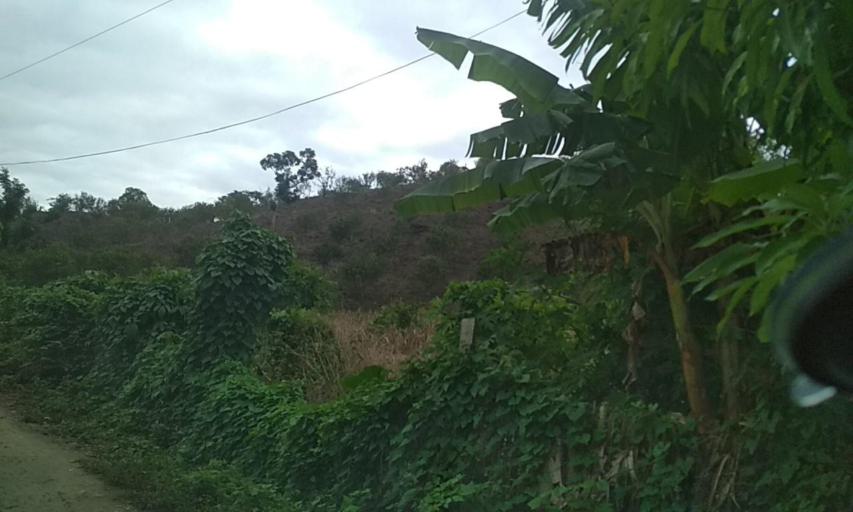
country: MX
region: Veracruz
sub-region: Papantla
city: Polutla
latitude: 20.5867
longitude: -97.2787
